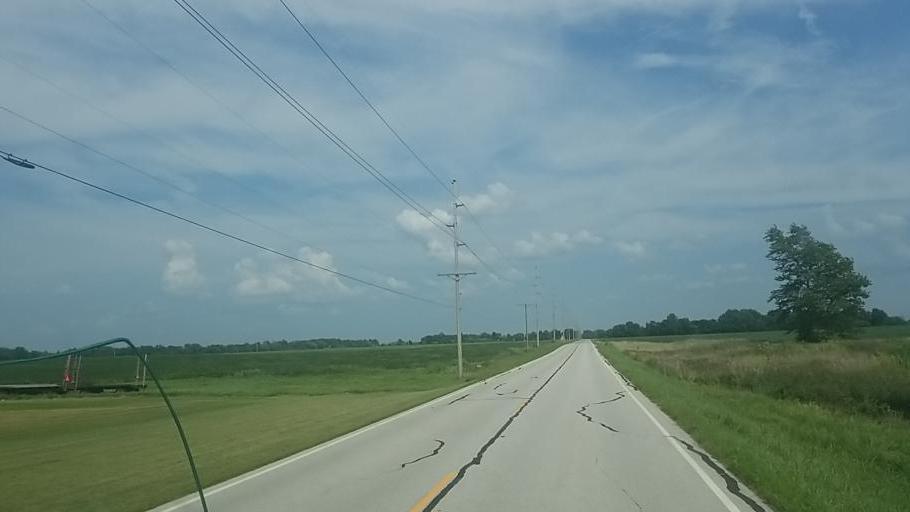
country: US
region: Ohio
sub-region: Hardin County
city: Forest
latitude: 40.7819
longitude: -83.5449
